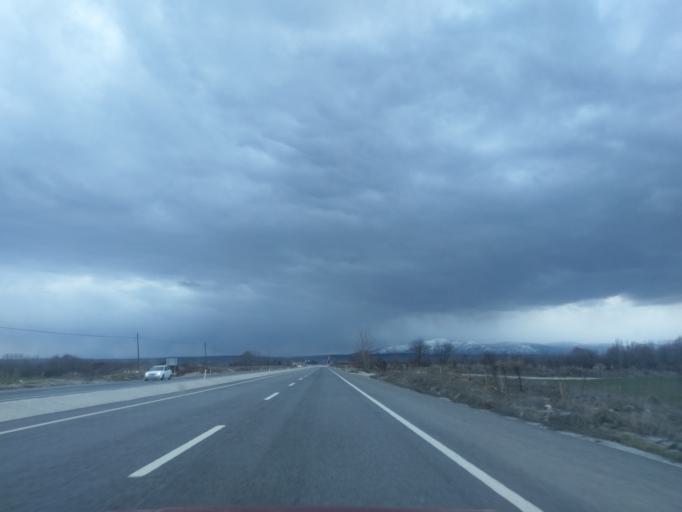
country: TR
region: Kuetahya
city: Cavdarhisar
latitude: 39.2093
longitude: 29.6451
